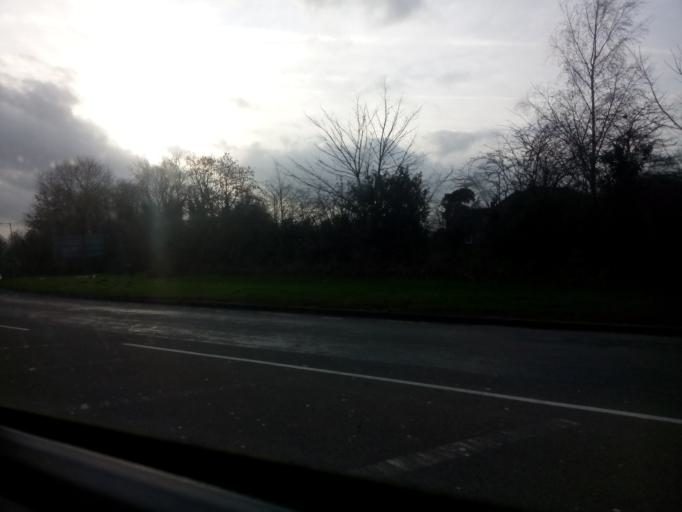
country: GB
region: England
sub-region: Worcestershire
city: Bromsgrove
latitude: 52.3760
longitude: -2.0468
